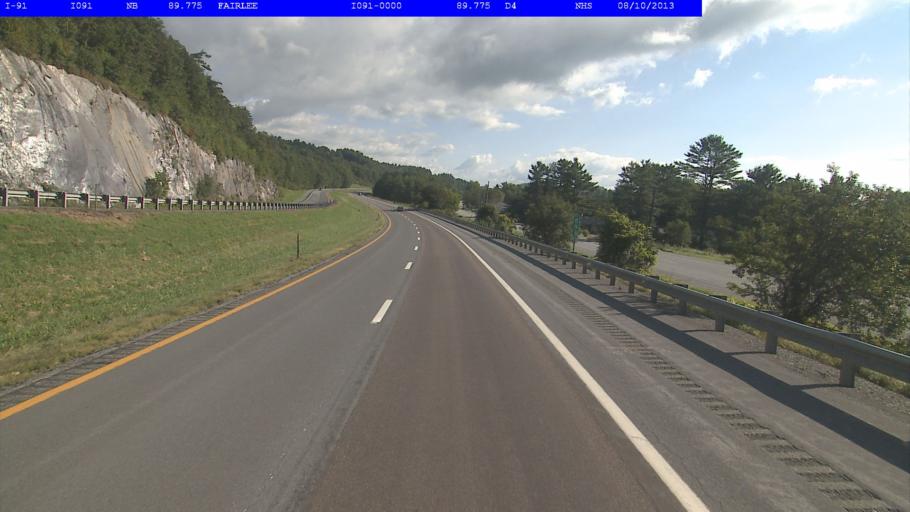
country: US
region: New Hampshire
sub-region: Grafton County
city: Orford
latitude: 43.8869
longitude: -72.1749
